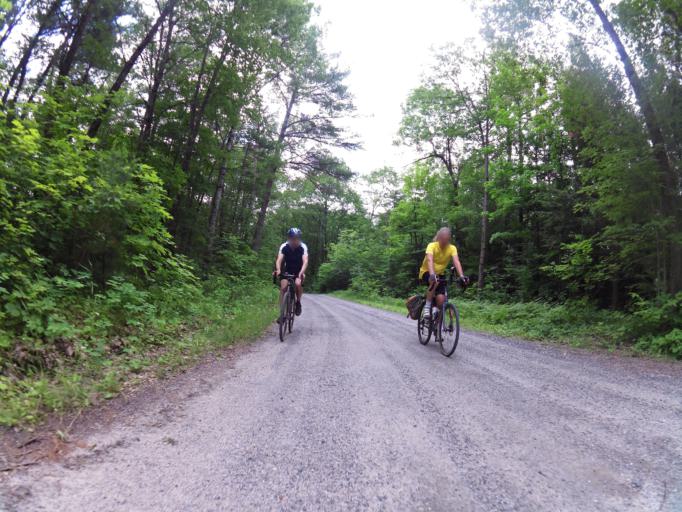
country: CA
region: Ontario
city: Perth
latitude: 45.0251
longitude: -76.5357
